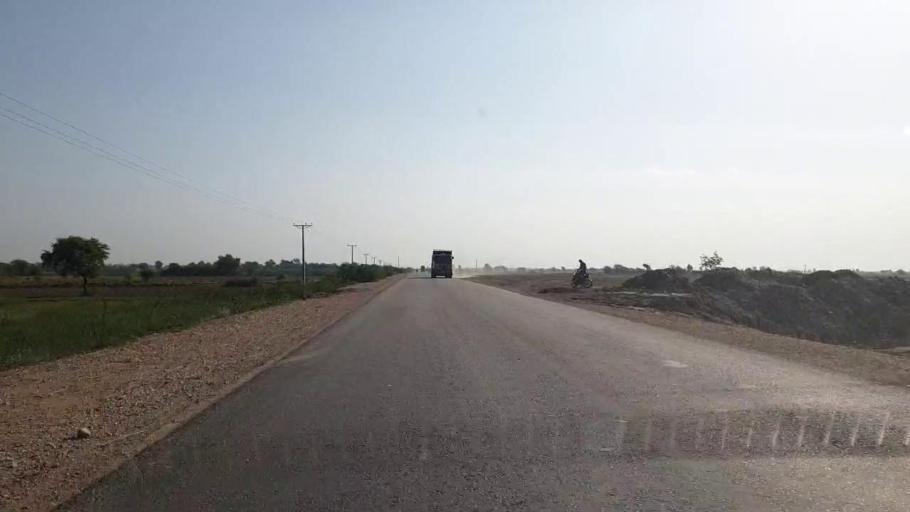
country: PK
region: Sindh
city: Tando Bago
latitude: 24.6576
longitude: 68.9875
